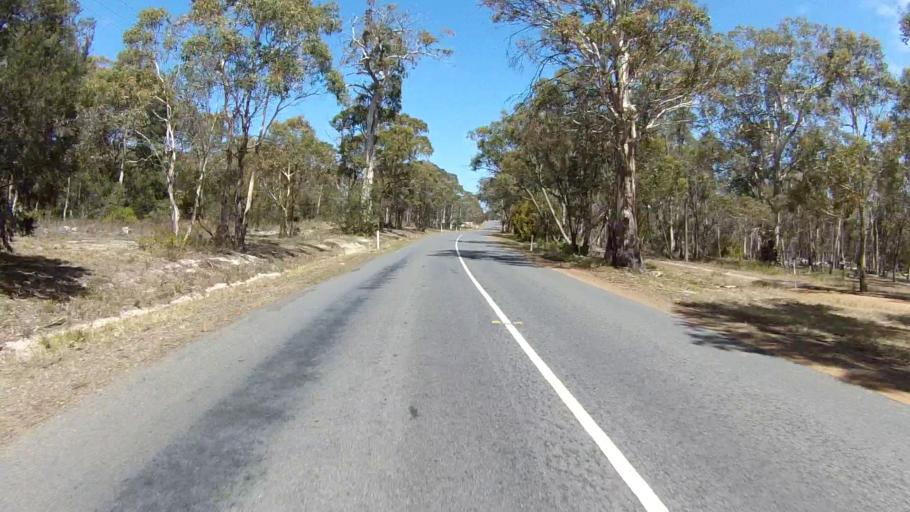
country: AU
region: Tasmania
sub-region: Clarence
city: Sandford
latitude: -42.9711
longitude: 147.4800
